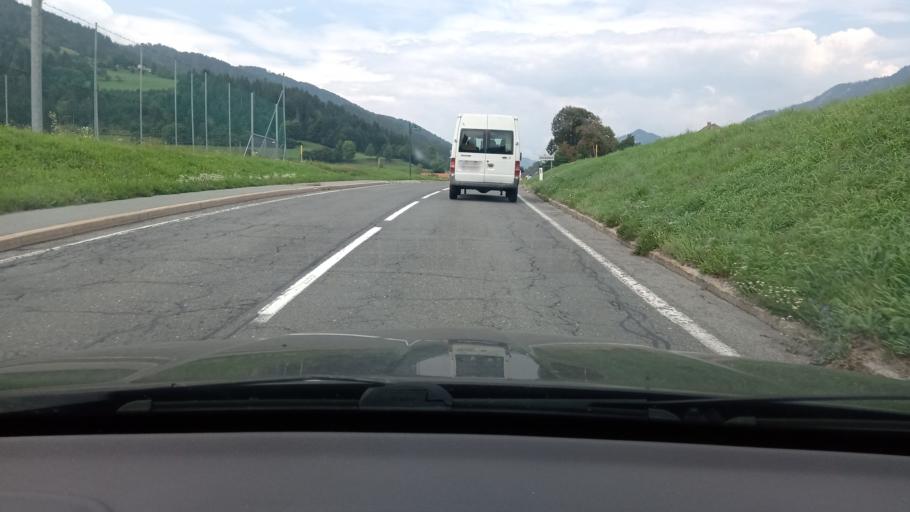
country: AT
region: Carinthia
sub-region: Politischer Bezirk Hermagor
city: Hermagor
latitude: 46.6302
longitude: 13.3587
